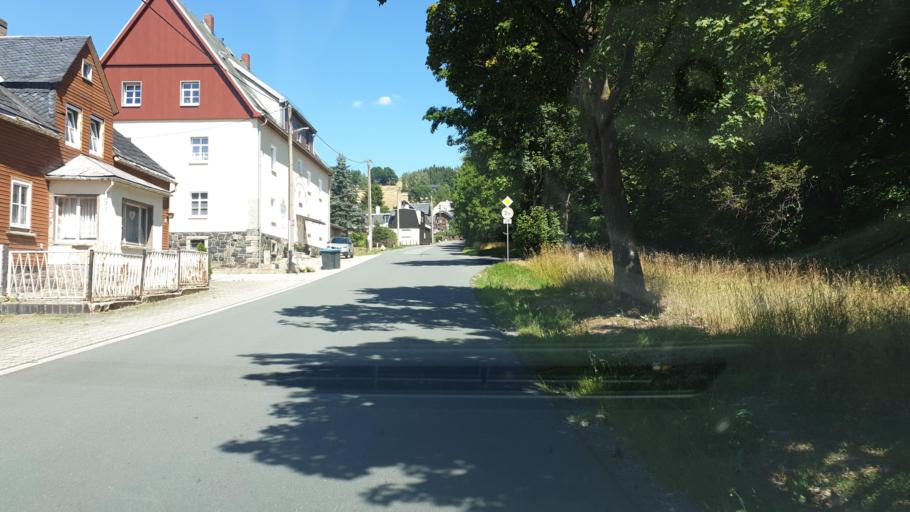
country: DE
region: Saxony
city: Klingenthal
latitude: 50.3800
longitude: 12.4970
